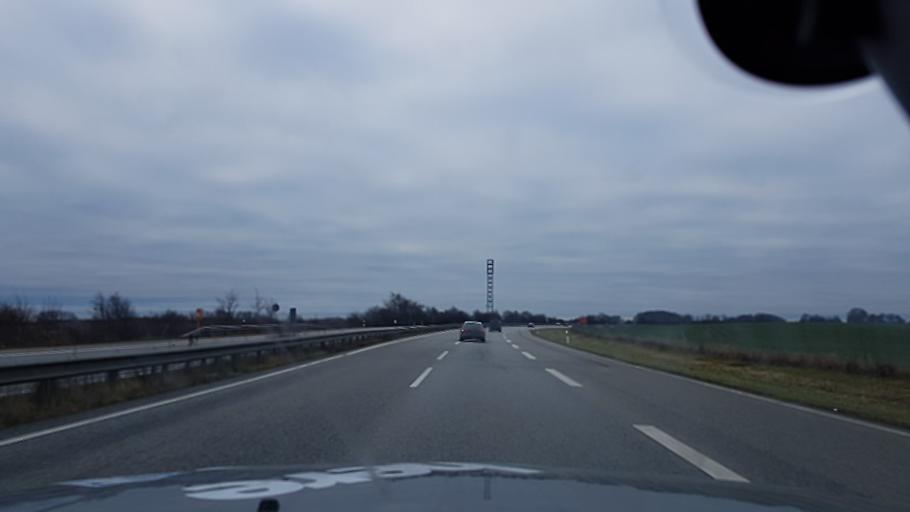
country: DE
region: Schleswig-Holstein
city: Gremersdorf
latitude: 54.3282
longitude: 10.9320
